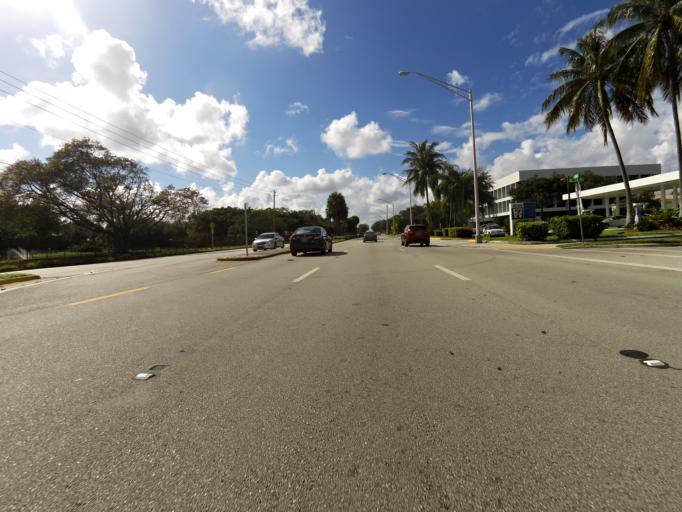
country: US
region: Florida
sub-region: Broward County
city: Hollywood
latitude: 26.0330
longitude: -80.1778
